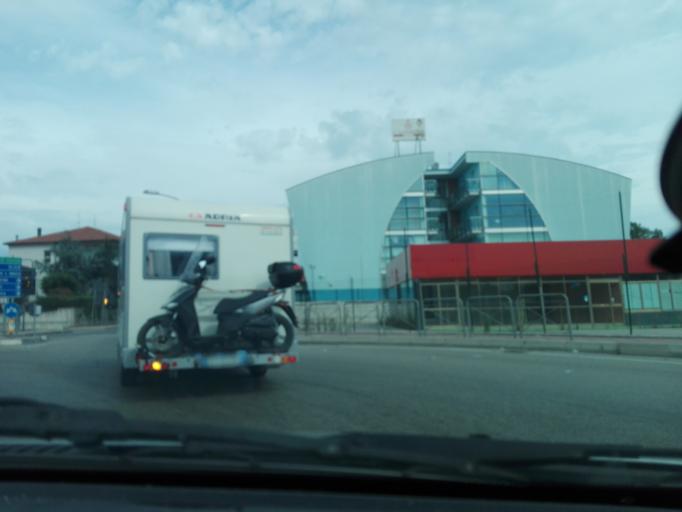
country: IT
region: Abruzzo
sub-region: Provincia di Pescara
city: Montesilvano Marina
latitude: 42.5231
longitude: 14.1422
